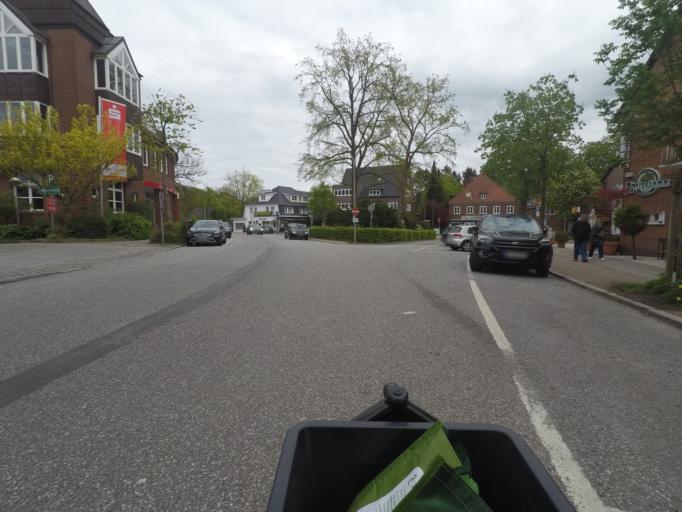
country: DE
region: Hamburg
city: Bergstedt
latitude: 53.6489
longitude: 10.1667
